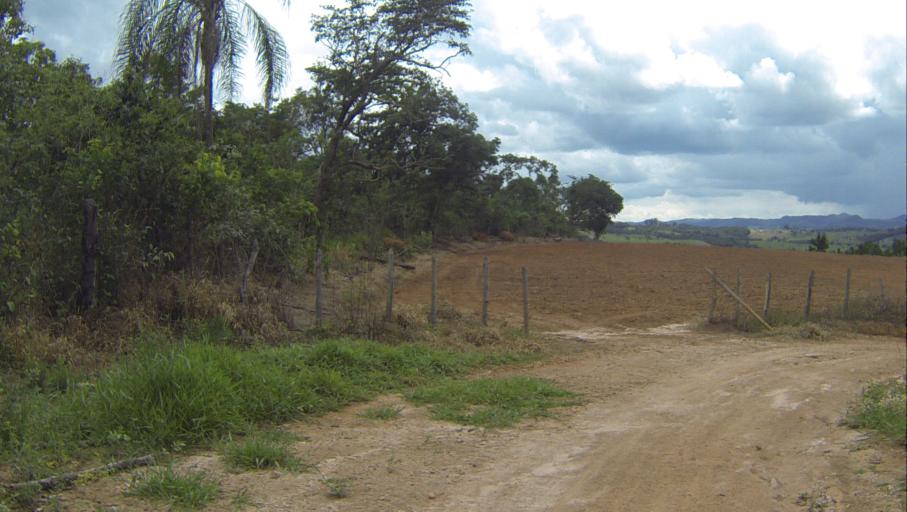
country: BR
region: Minas Gerais
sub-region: Brumadinho
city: Brumadinho
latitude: -20.1503
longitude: -44.1195
